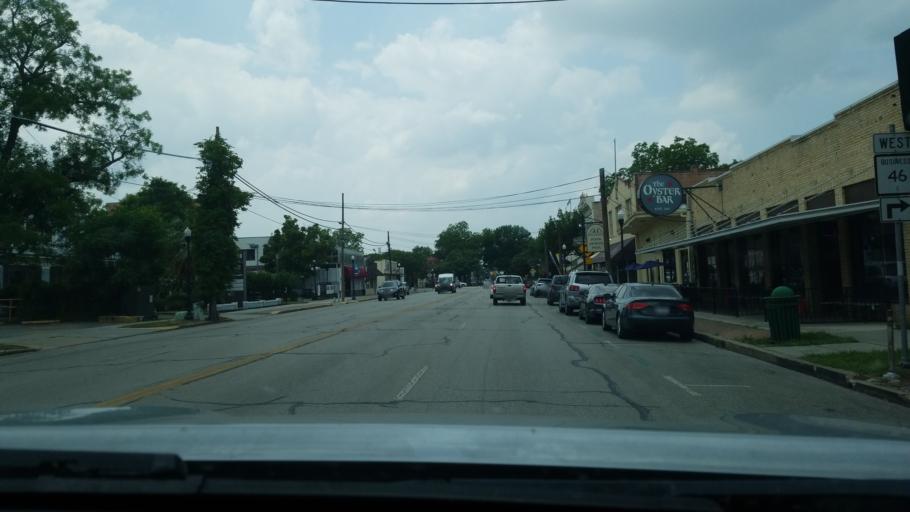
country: US
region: Texas
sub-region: Comal County
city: New Braunfels
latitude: 29.7019
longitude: -98.1230
